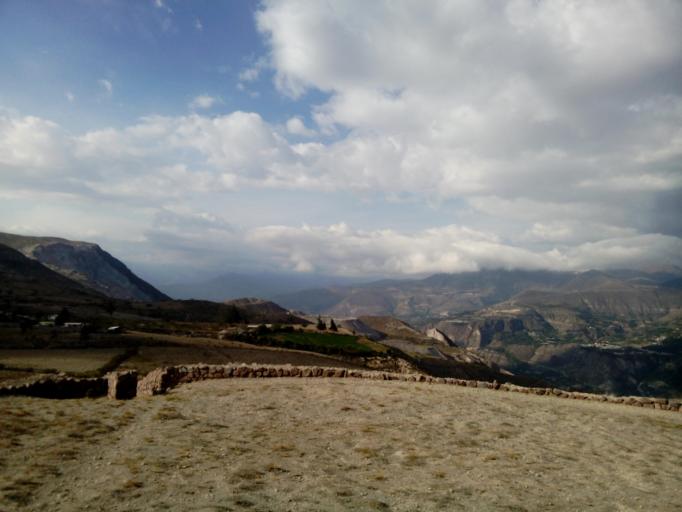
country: EC
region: Pichincha
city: Quito
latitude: 0.0147
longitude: -78.4305
